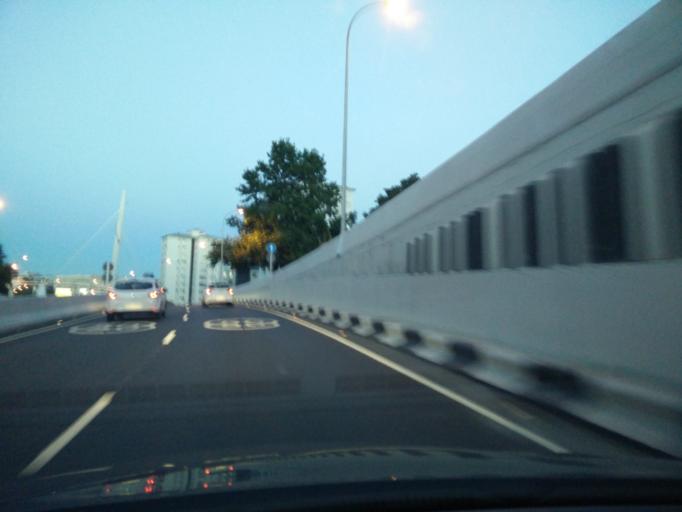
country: ES
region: Galicia
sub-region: Provincia da Coruna
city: A Coruna
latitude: 43.3431
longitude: -8.4130
